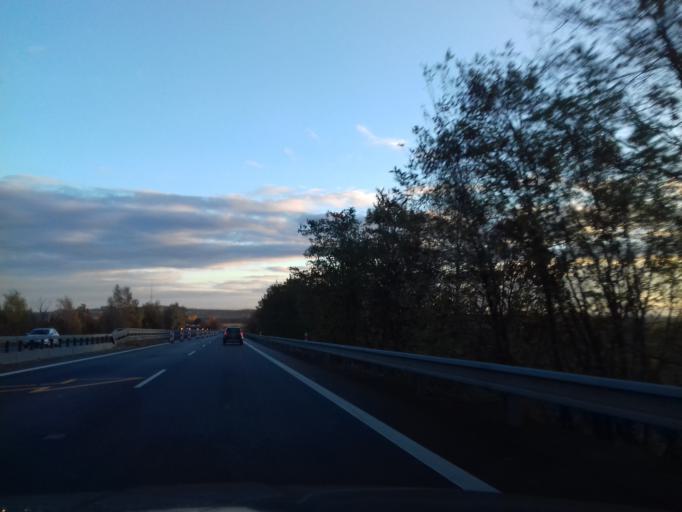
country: CZ
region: Olomoucky
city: Otaslavice
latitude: 49.3581
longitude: 17.0848
